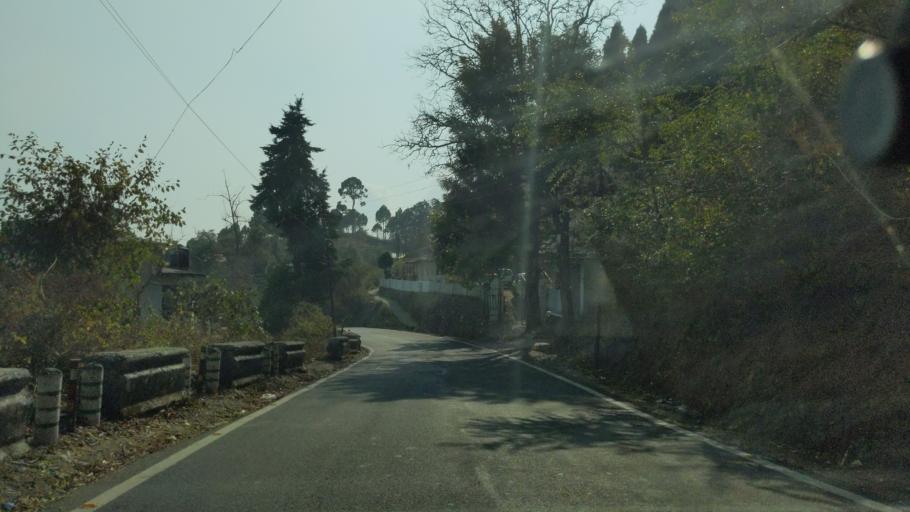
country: IN
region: Uttarakhand
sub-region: Naini Tal
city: Bhowali
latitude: 29.3791
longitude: 79.5179
